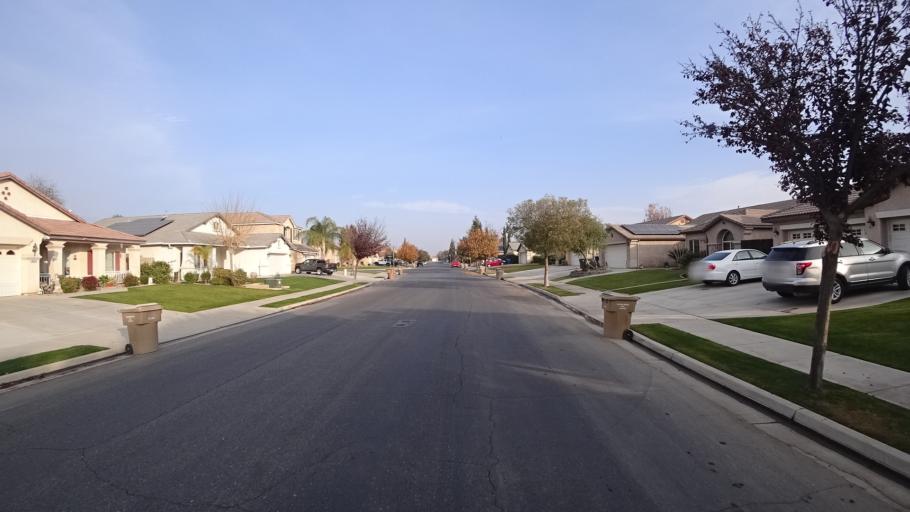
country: US
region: California
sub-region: Kern County
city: Greenacres
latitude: 35.4225
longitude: -119.1270
